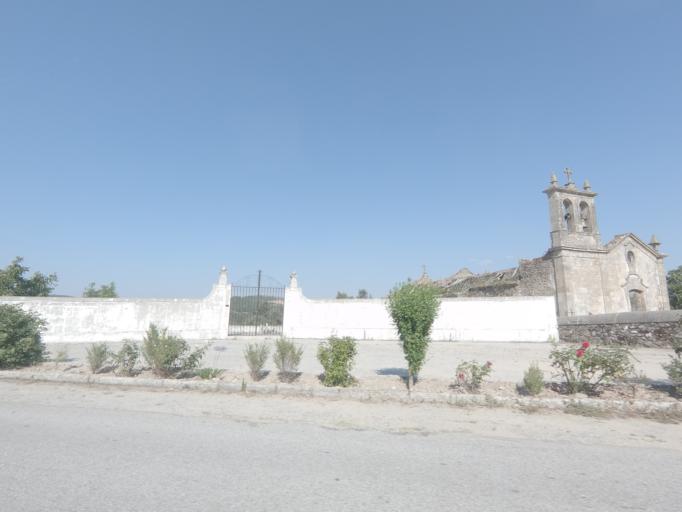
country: PT
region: Viseu
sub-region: Moimenta da Beira
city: Moimenta da Beira
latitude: 40.9734
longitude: -7.5914
